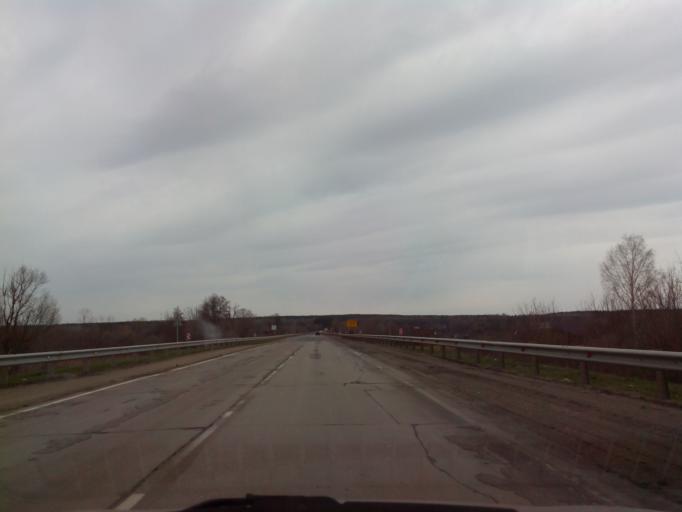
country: RU
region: Tambov
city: Znamenka
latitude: 52.5237
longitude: 41.3615
